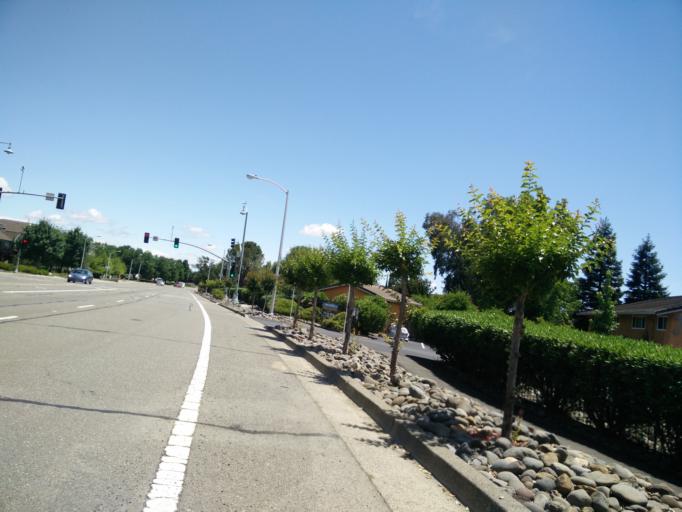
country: US
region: California
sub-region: Shasta County
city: Redding
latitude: 40.6013
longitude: -122.3738
